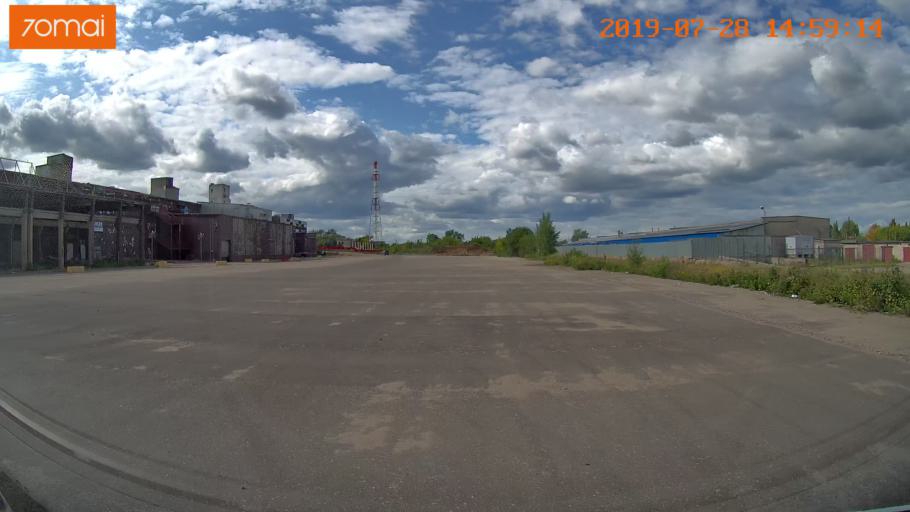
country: RU
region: Ivanovo
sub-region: Gorod Ivanovo
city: Ivanovo
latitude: 56.9677
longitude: 41.0259
